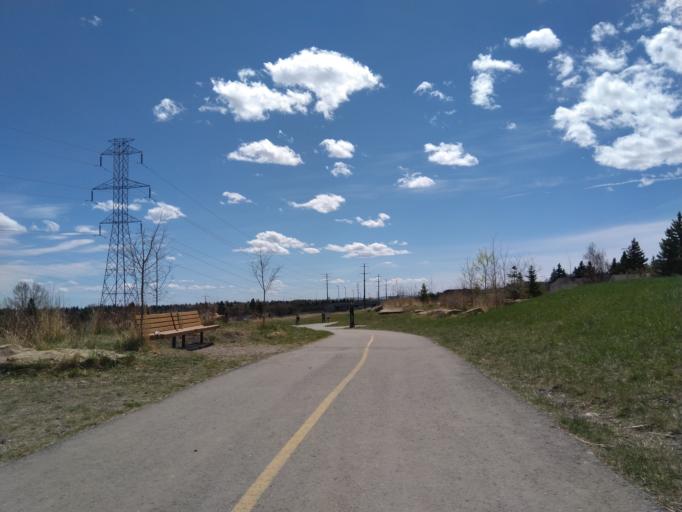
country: CA
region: Alberta
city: Calgary
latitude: 51.0452
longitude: -114.1653
